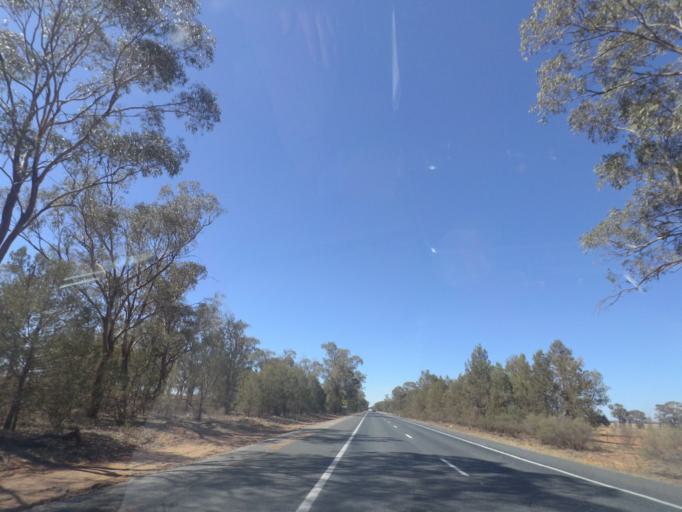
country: AU
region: New South Wales
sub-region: Bland
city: West Wyalong
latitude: -34.2125
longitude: 147.1084
